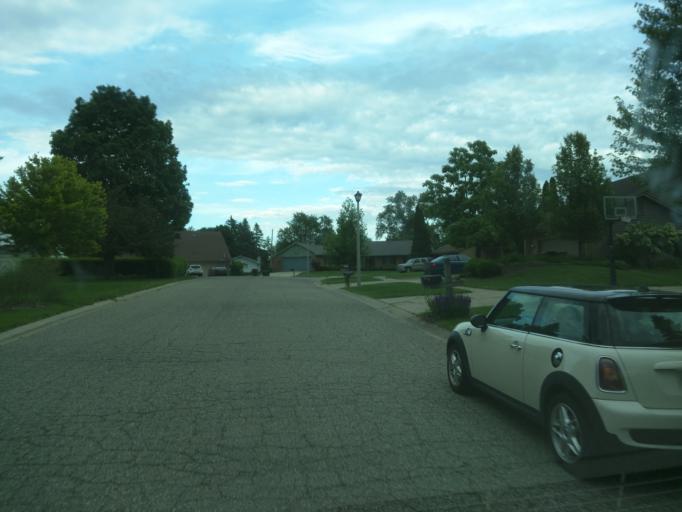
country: US
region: Michigan
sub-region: Eaton County
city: Waverly
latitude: 42.7505
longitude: -84.6189
